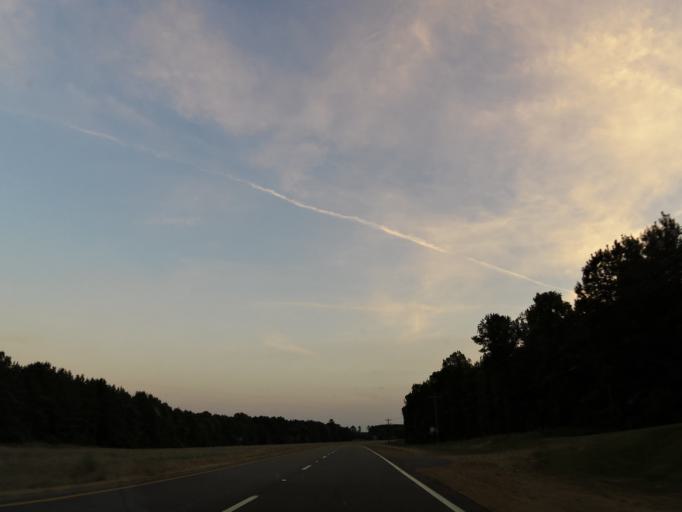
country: US
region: Mississippi
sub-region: Kemper County
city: De Kalb
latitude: 32.7399
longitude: -88.4669
